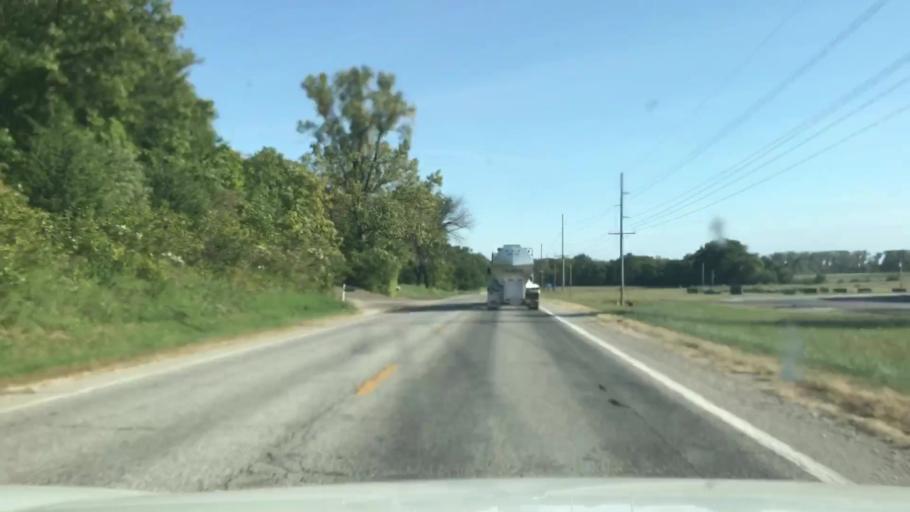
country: US
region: Illinois
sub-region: Adams County
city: Quincy
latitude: 39.8494
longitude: -91.3785
